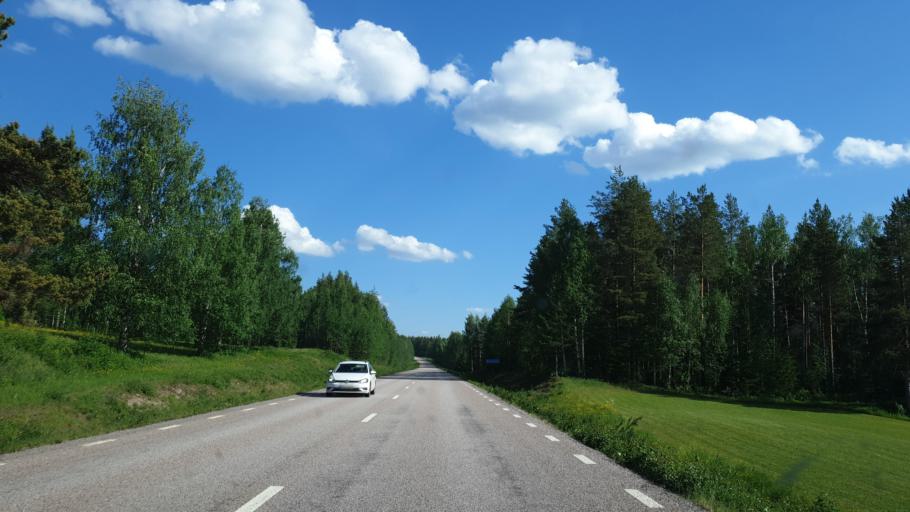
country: SE
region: Norrbotten
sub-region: Alvsbyns Kommun
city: AElvsbyn
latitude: 65.7906
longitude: 20.6603
